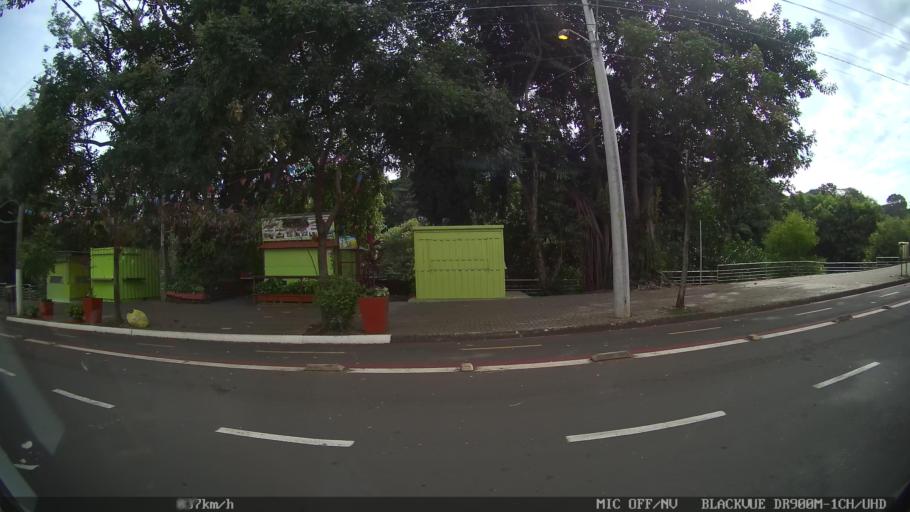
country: BR
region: Sao Paulo
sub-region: Piracicaba
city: Piracicaba
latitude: -22.7174
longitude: -47.6531
